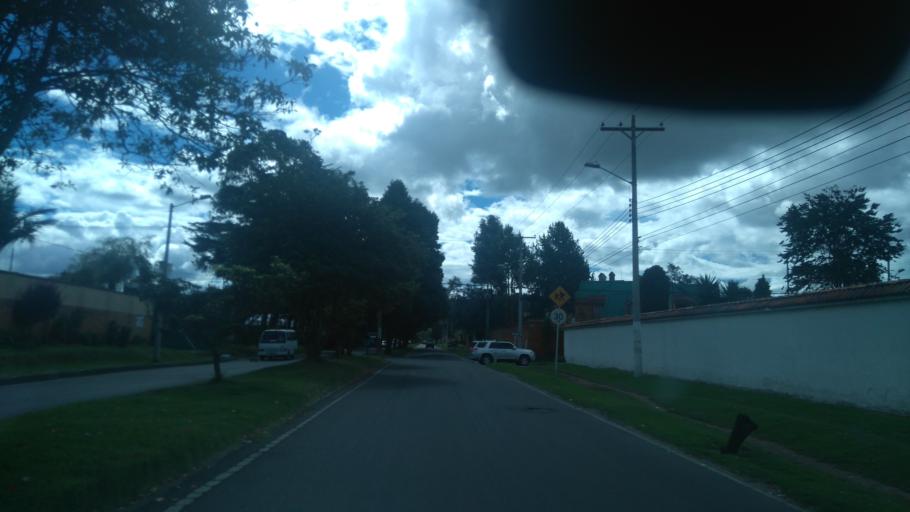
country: CO
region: Cundinamarca
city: Cota
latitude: 4.7601
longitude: -74.0573
